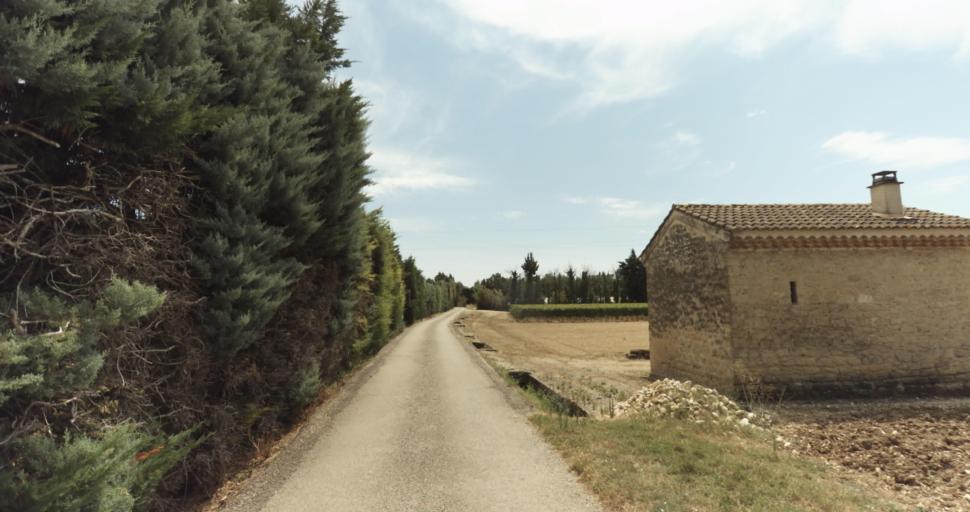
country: FR
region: Provence-Alpes-Cote d'Azur
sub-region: Departement du Vaucluse
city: Loriol-du-Comtat
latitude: 44.0584
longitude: 5.0155
